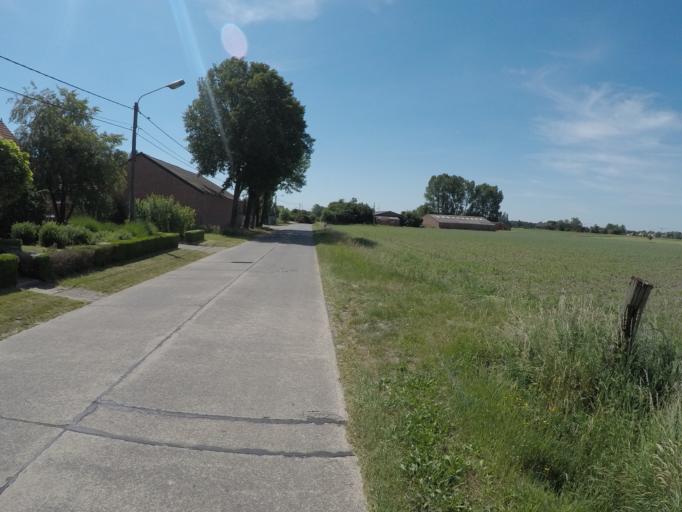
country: NL
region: North Brabant
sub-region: Gemeente Zundert
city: Zundert
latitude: 51.4109
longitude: 4.6617
